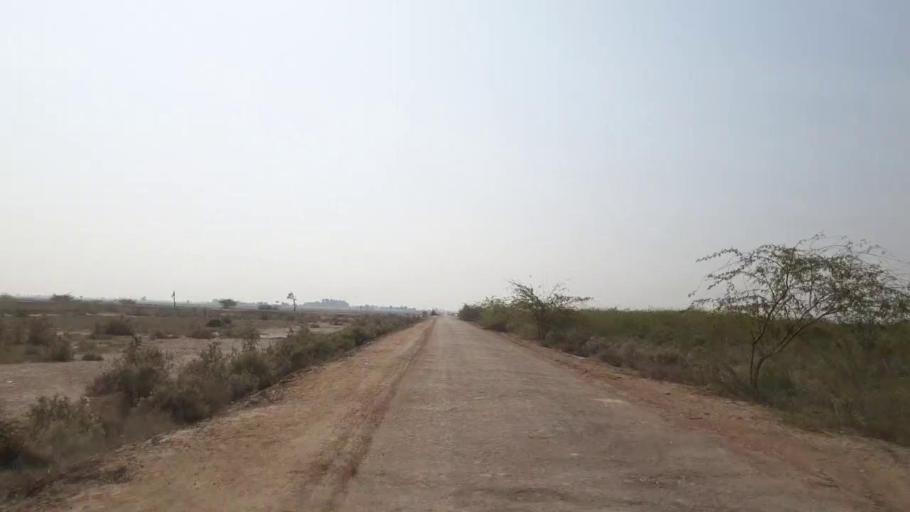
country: PK
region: Sindh
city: Mirpur Khas
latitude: 25.5843
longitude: 69.0254
